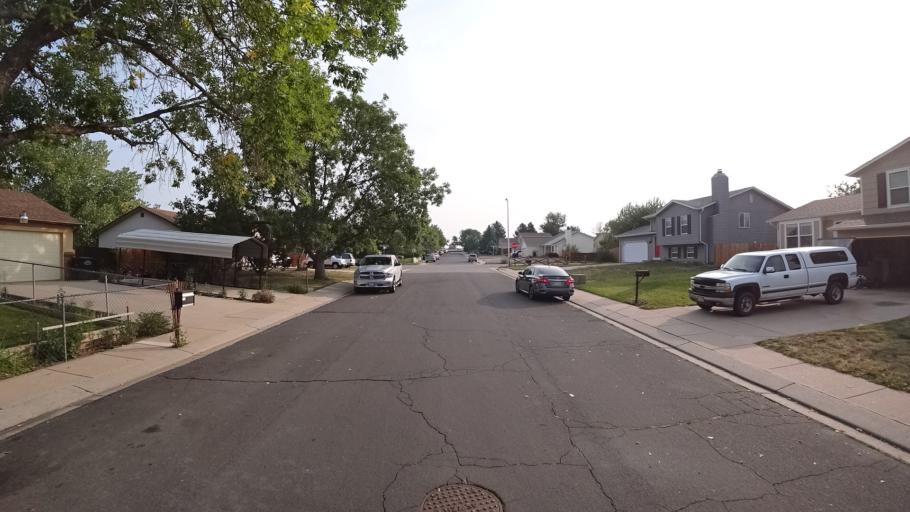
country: US
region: Colorado
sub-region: El Paso County
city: Stratmoor
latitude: 38.8032
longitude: -104.7449
